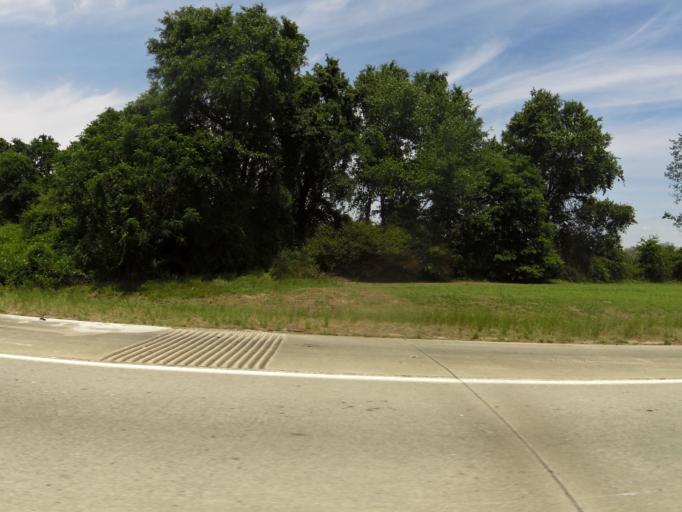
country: US
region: Georgia
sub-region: Bulloch County
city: Statesboro
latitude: 32.2877
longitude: -81.7962
